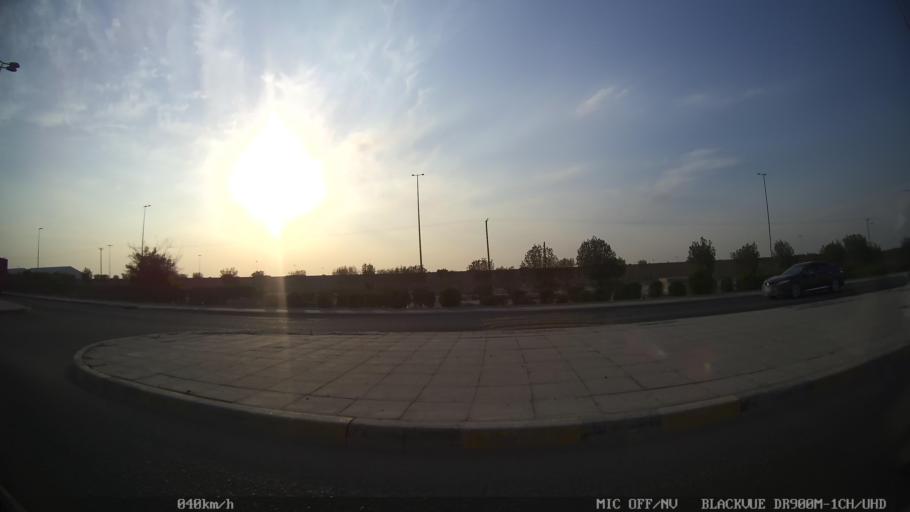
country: KW
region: Al Farwaniyah
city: Janub as Surrah
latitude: 29.2510
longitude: 48.0104
